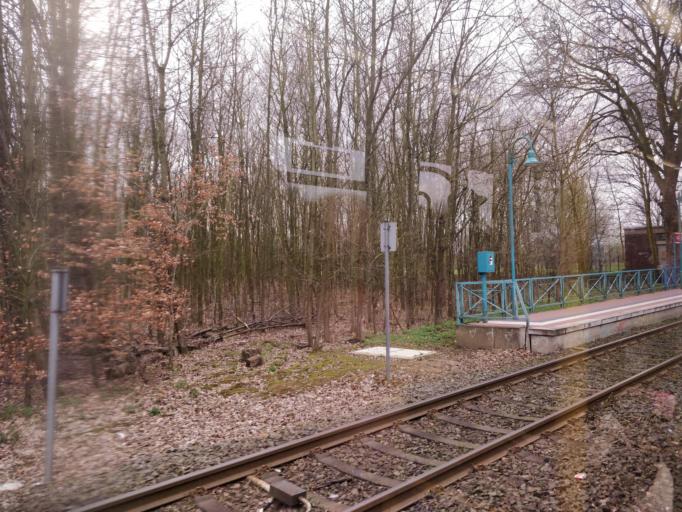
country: DE
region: North Rhine-Westphalia
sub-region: Regierungsbezirk Koln
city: Hurth
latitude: 50.9200
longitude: 6.8778
